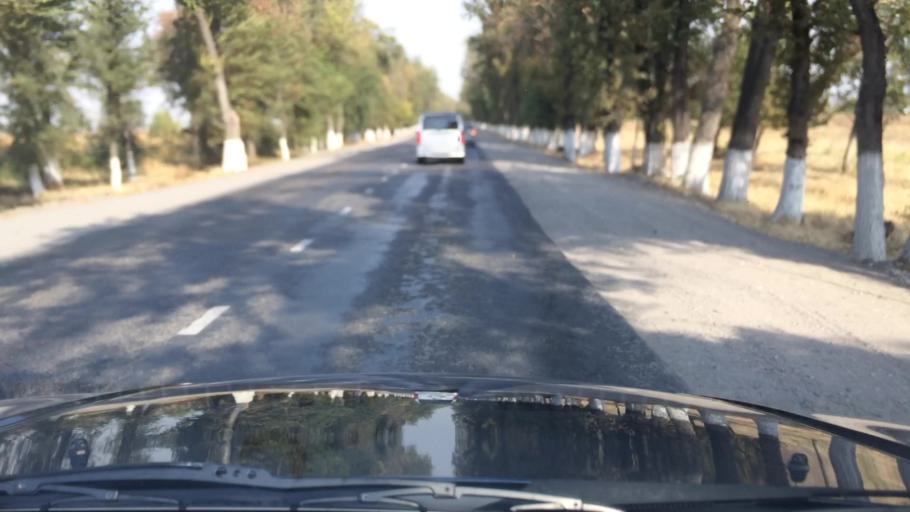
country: KG
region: Chuy
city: Lebedinovka
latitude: 42.9266
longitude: 74.6907
